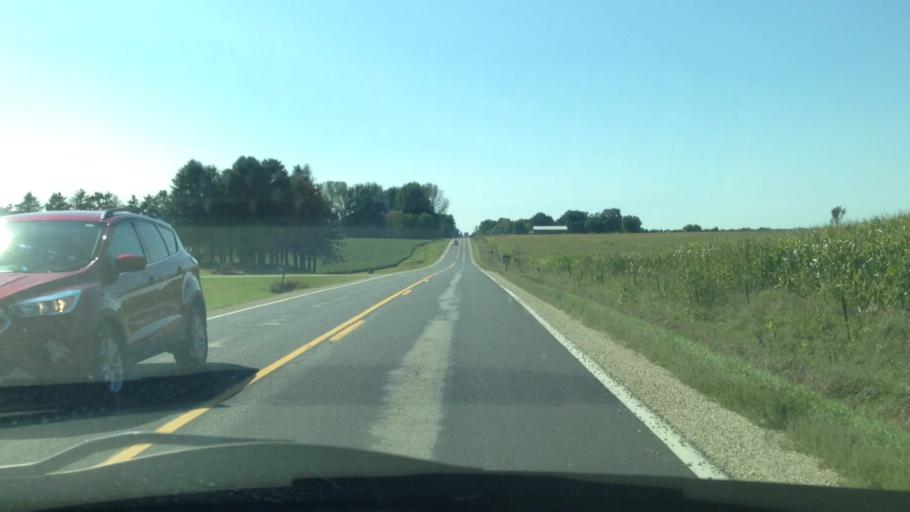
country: US
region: Minnesota
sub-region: Winona County
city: Lewiston
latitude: 43.9404
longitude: -91.7813
